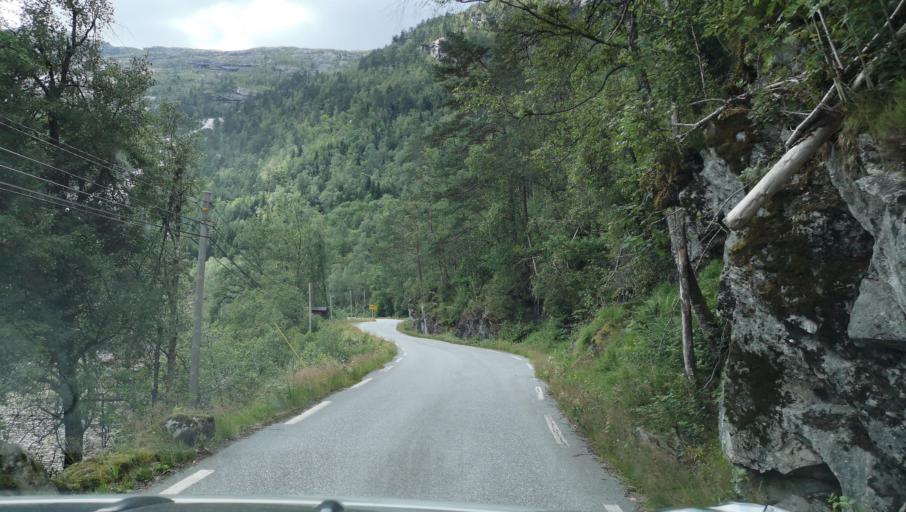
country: NO
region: Hordaland
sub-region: Modalen
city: Mo
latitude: 60.7855
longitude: 5.8431
